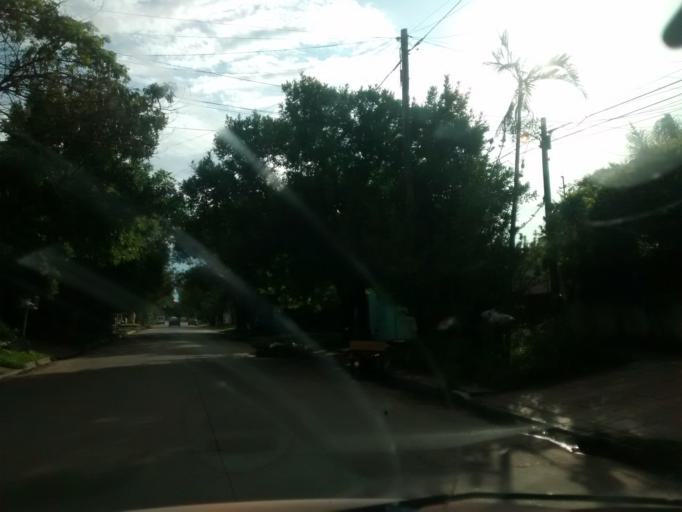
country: AR
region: Chaco
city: Resistencia
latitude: -27.4458
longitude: -58.9736
